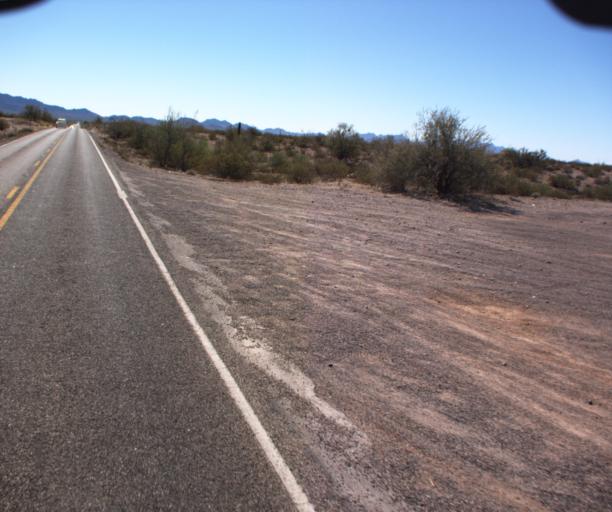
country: US
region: Arizona
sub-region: Pima County
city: Ajo
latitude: 32.3529
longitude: -112.8218
